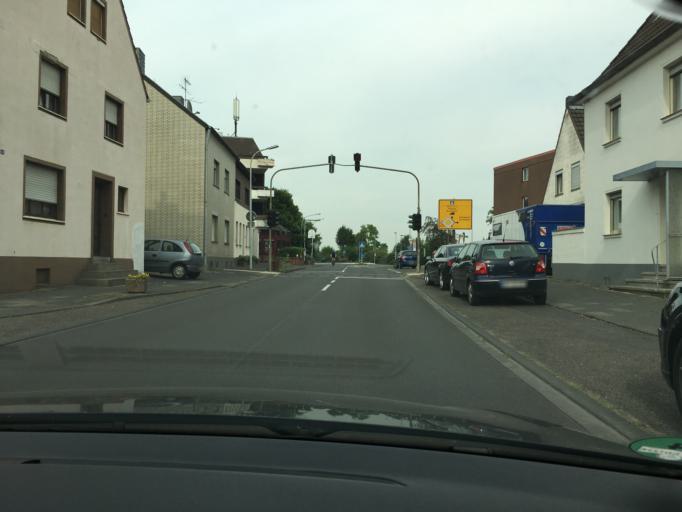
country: DE
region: North Rhine-Westphalia
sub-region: Regierungsbezirk Koln
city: Pulheim
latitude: 50.9666
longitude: 6.7534
